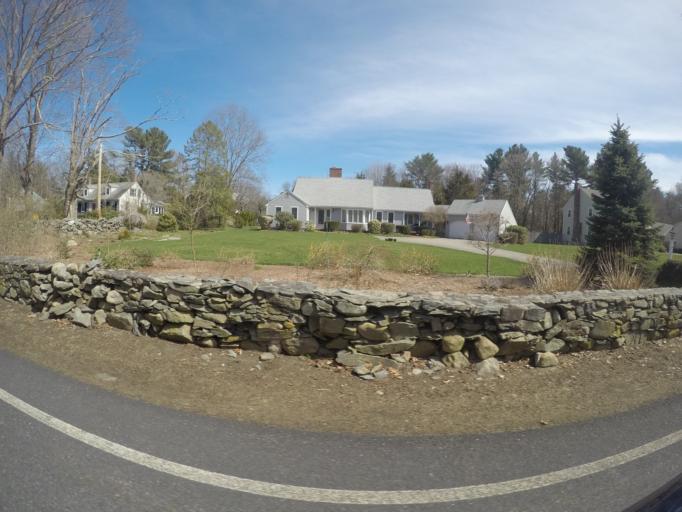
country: US
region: Massachusetts
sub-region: Bristol County
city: Easton
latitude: 42.0216
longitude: -71.0934
